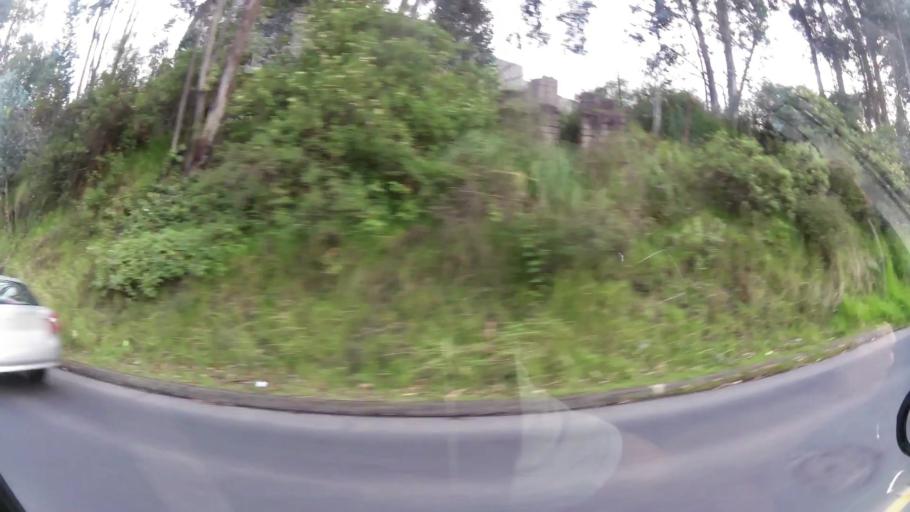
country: EC
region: Pichincha
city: Quito
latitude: -0.2631
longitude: -78.4946
